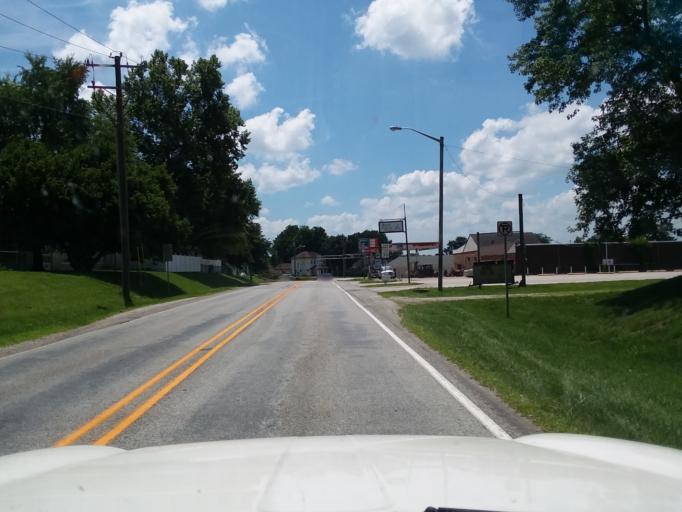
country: US
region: Indiana
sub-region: Johnson County
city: Trafalgar
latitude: 39.3720
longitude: -86.2563
